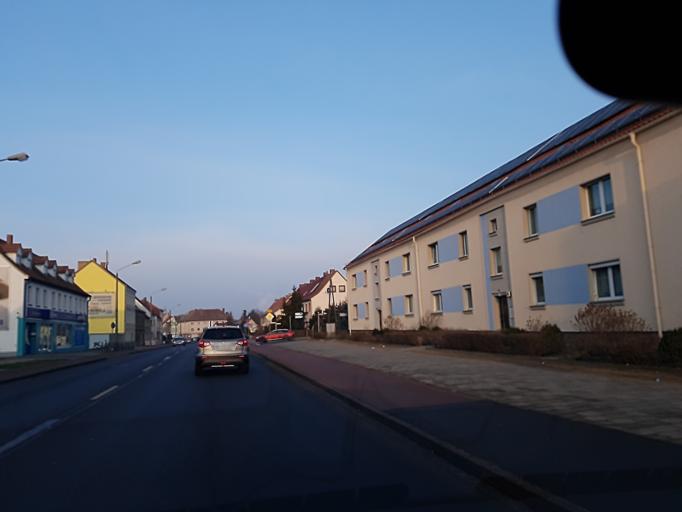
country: DE
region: Saxony-Anhalt
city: Wittenburg
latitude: 51.8669
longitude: 12.6058
